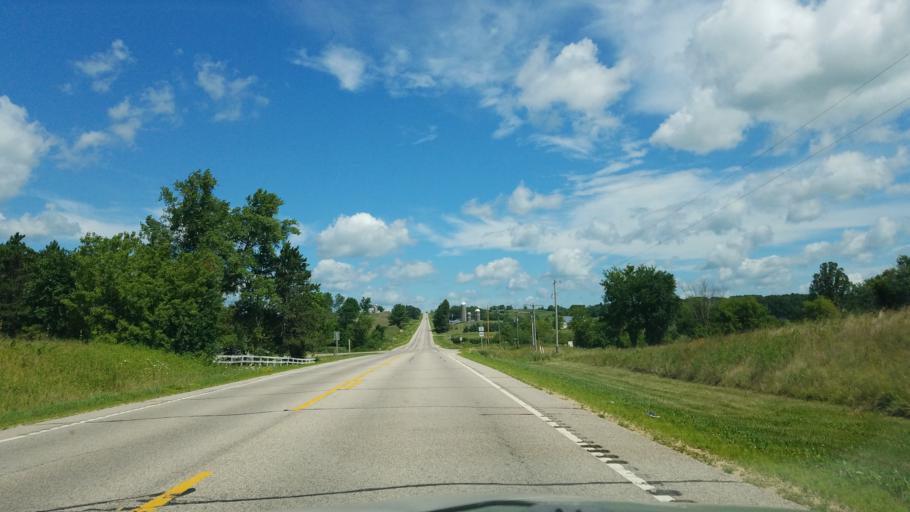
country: US
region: Wisconsin
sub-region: Saint Croix County
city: Glenwood City
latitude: 45.0011
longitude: -92.1966
